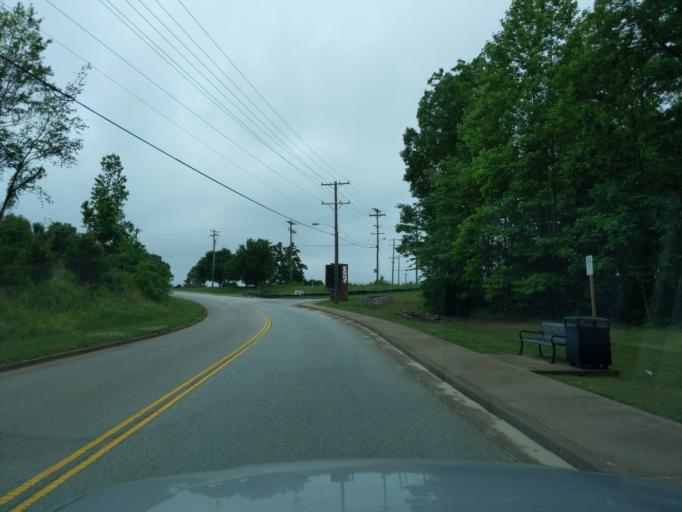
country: US
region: South Carolina
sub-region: Greenville County
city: Five Forks
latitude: 34.8607
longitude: -82.2170
